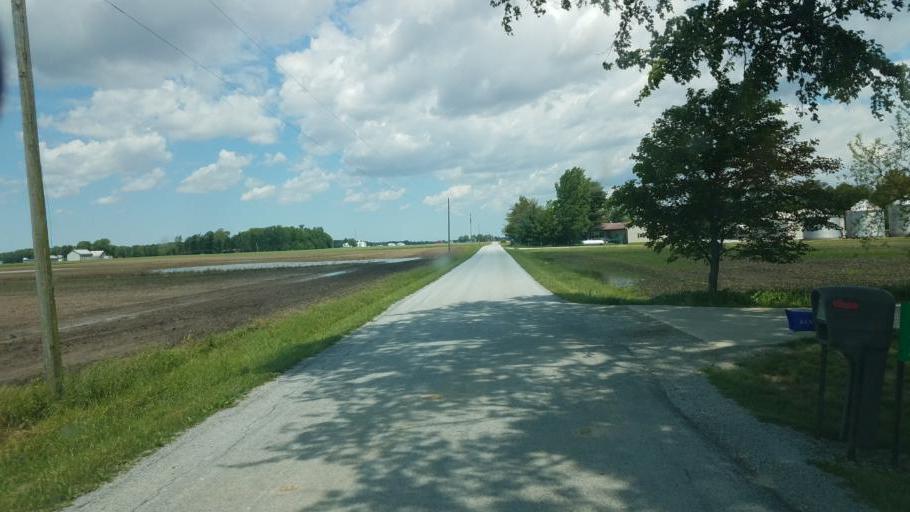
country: US
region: Ohio
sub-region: Hardin County
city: Forest
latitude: 40.6811
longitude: -83.4778
